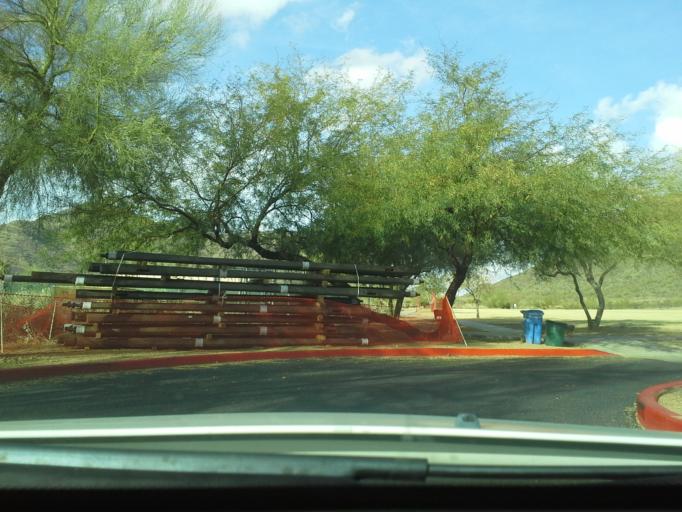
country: US
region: Arizona
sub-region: Maricopa County
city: Glendale
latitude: 33.5788
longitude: -112.0822
